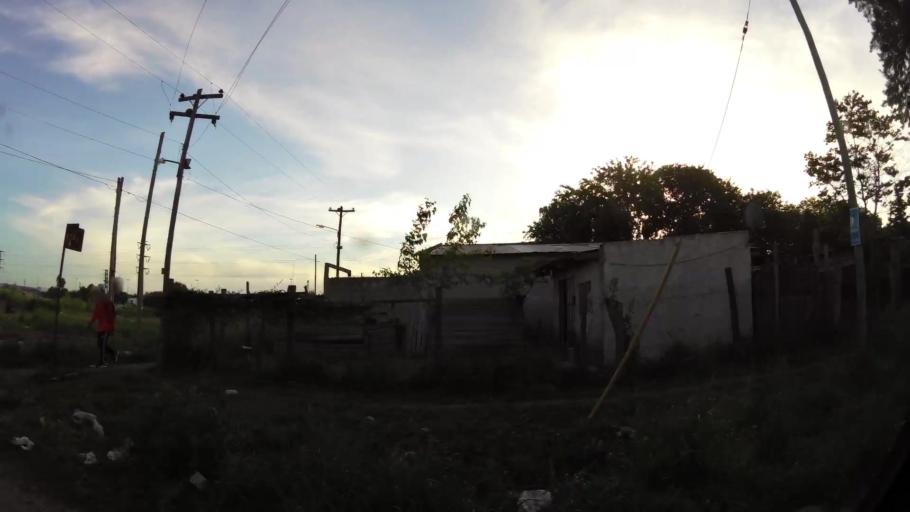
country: AR
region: Buenos Aires
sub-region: Partido de Quilmes
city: Quilmes
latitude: -34.7872
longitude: -58.2184
